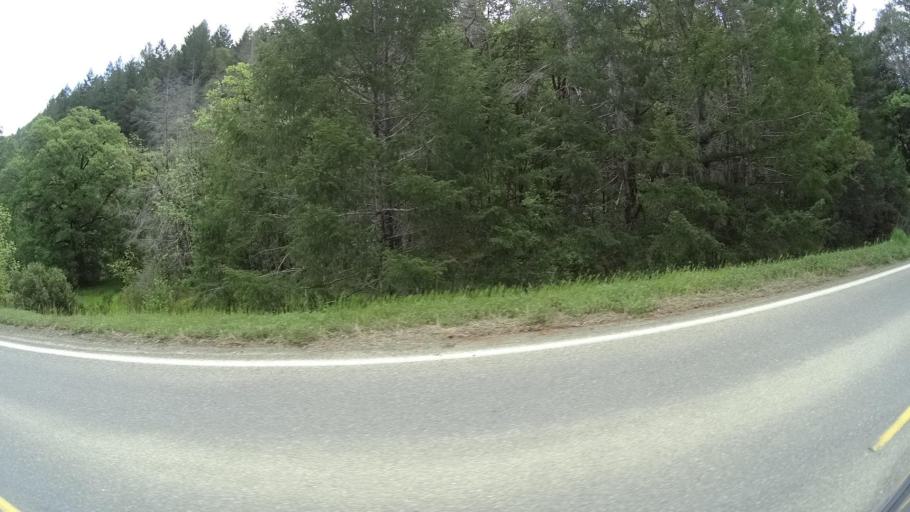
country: US
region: California
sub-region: Humboldt County
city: Redway
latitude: 40.1230
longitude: -123.8781
